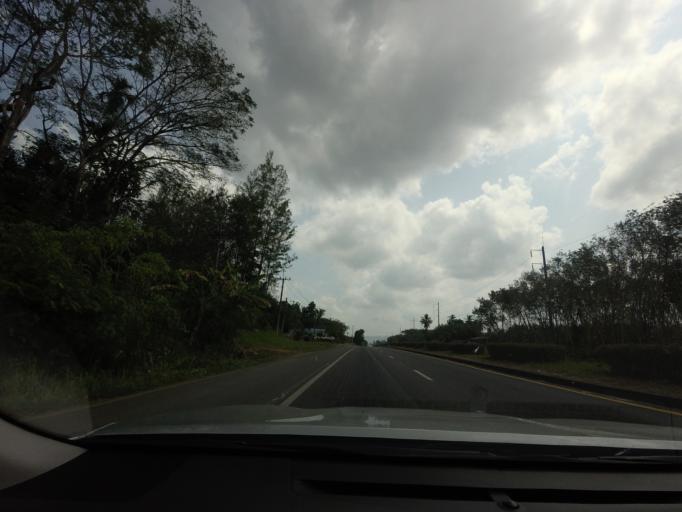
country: TH
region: Phangnga
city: Thap Put
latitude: 8.5089
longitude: 98.6564
